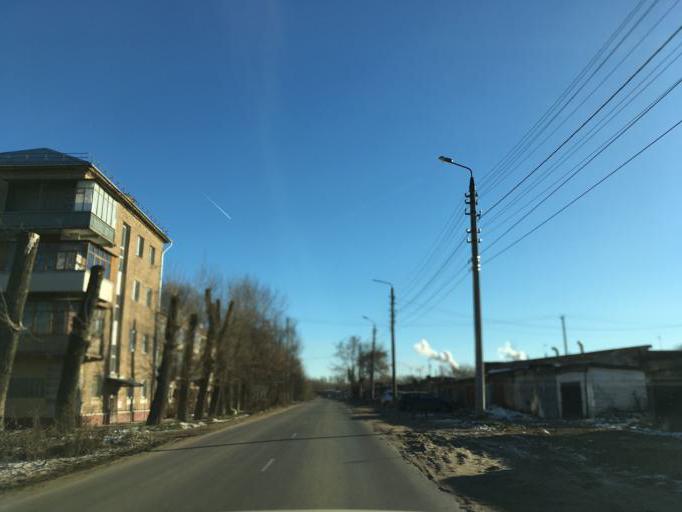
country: RU
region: Tula
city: Tula
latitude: 54.1807
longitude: 37.6989
